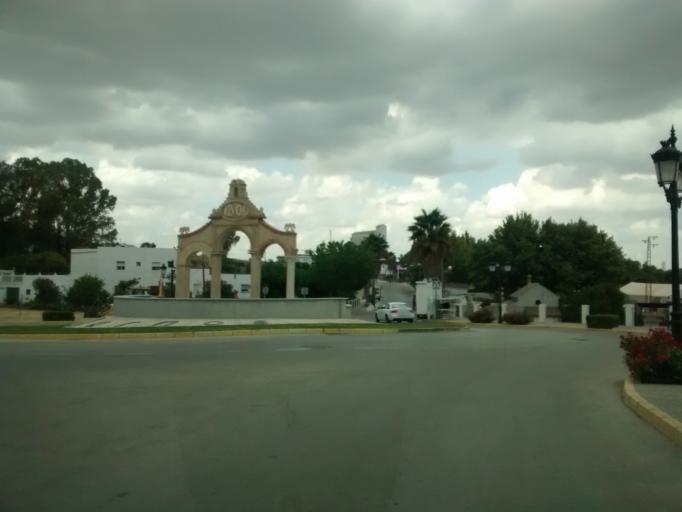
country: ES
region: Andalusia
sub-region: Provincia de Cadiz
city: Bornos
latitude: 36.8224
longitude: -5.7424
